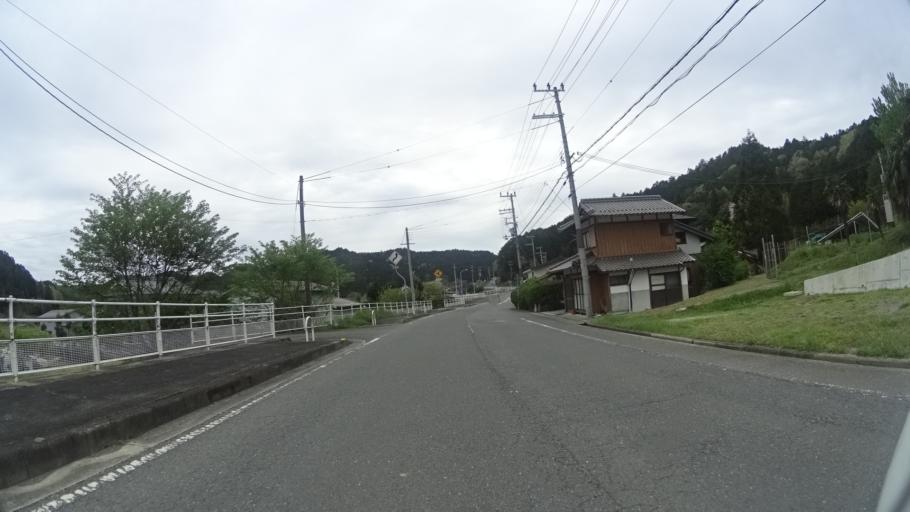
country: JP
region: Kyoto
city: Kameoka
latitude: 35.1933
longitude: 135.4624
